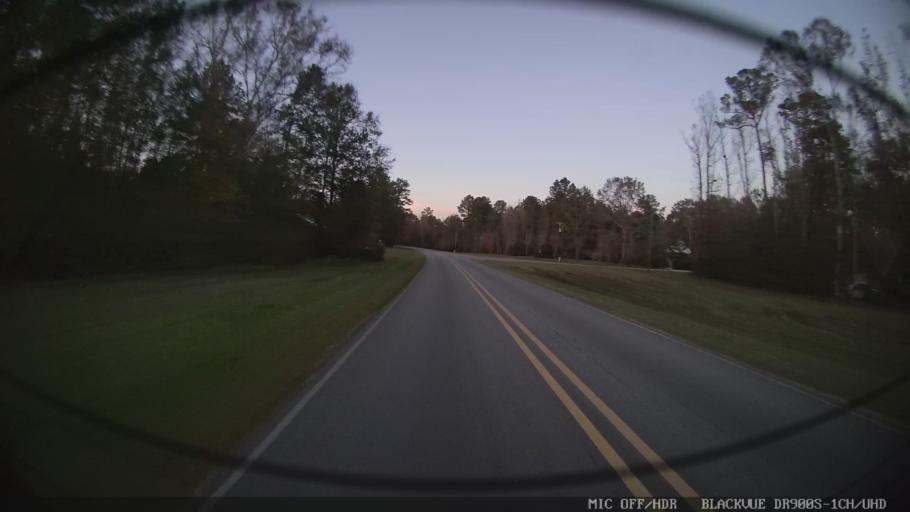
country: US
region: Mississippi
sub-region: Perry County
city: New Augusta
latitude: 31.0615
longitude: -89.1900
